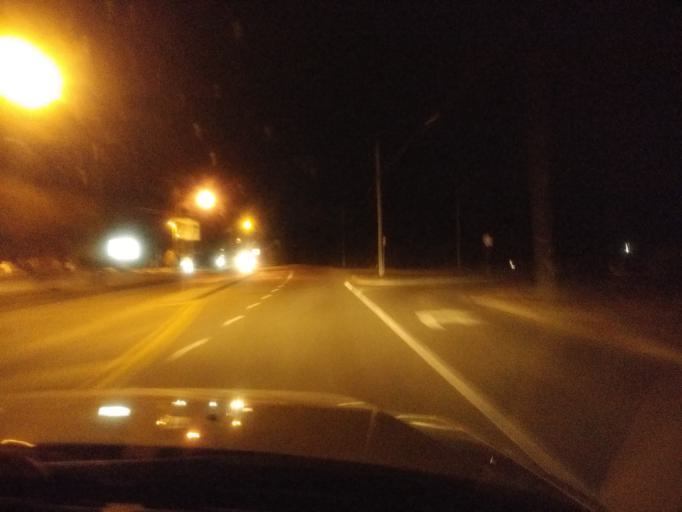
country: US
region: Virginia
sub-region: City of Chesapeake
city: Chesapeake
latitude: 36.7886
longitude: -76.1961
